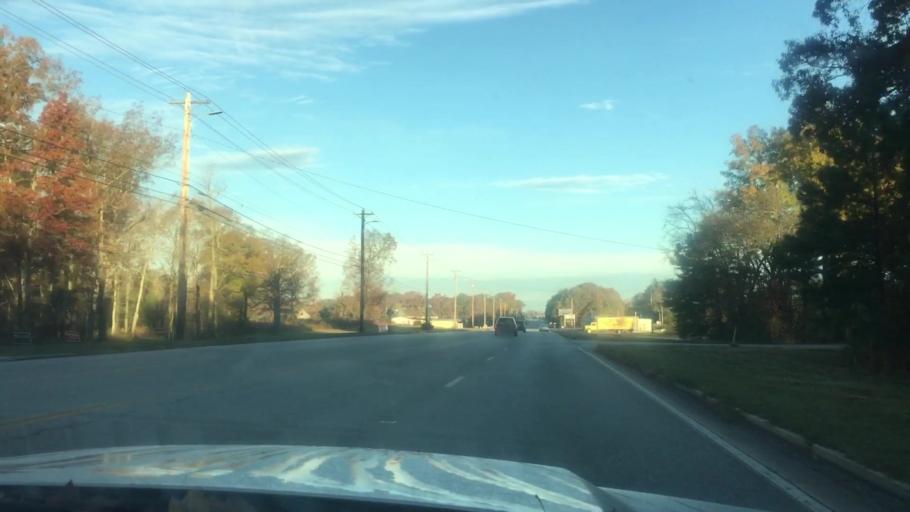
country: US
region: Tennessee
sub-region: Coffee County
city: Tullahoma
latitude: 35.3358
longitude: -86.1861
